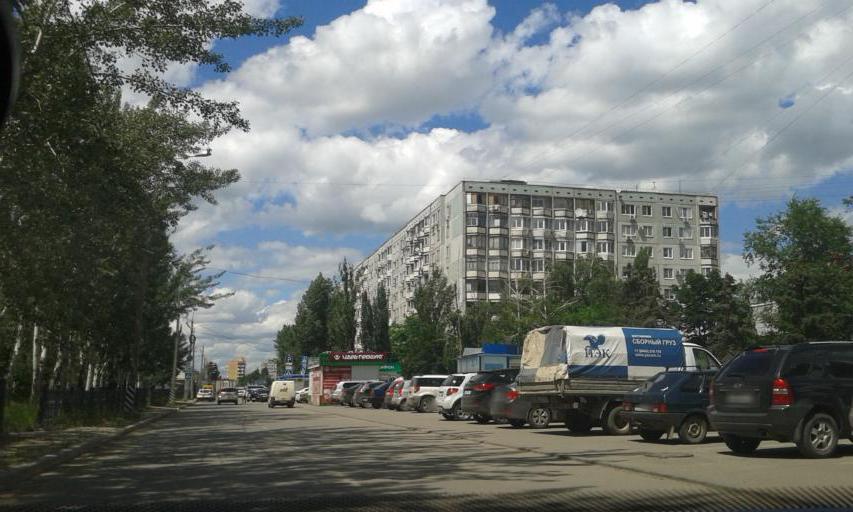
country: RU
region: Volgograd
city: Volgograd
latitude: 48.7556
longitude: 44.5027
